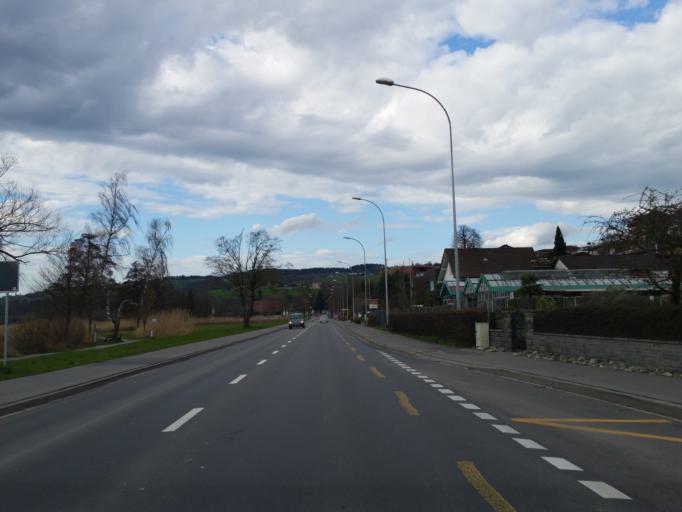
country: CH
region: Lucerne
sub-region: Sursee District
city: Sempach
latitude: 47.1292
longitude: 8.1924
